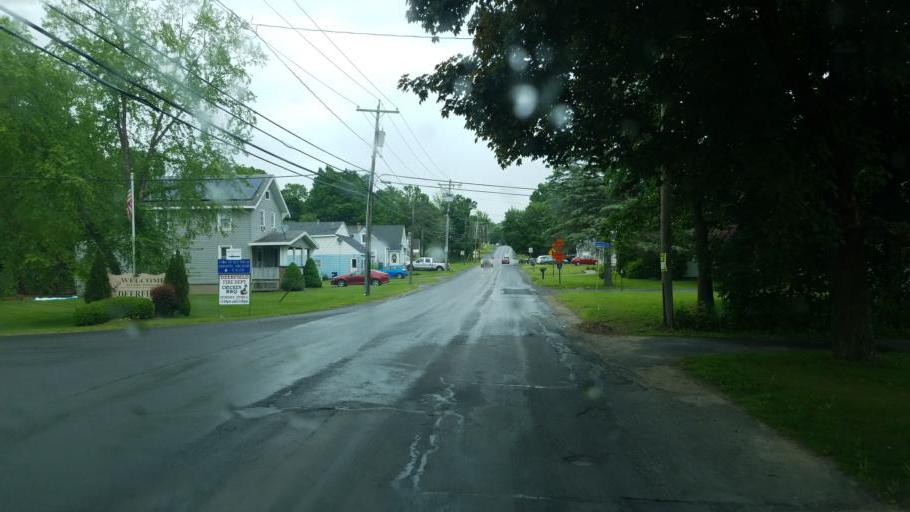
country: US
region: New York
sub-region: Oneida County
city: Utica
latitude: 43.1242
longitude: -75.2044
